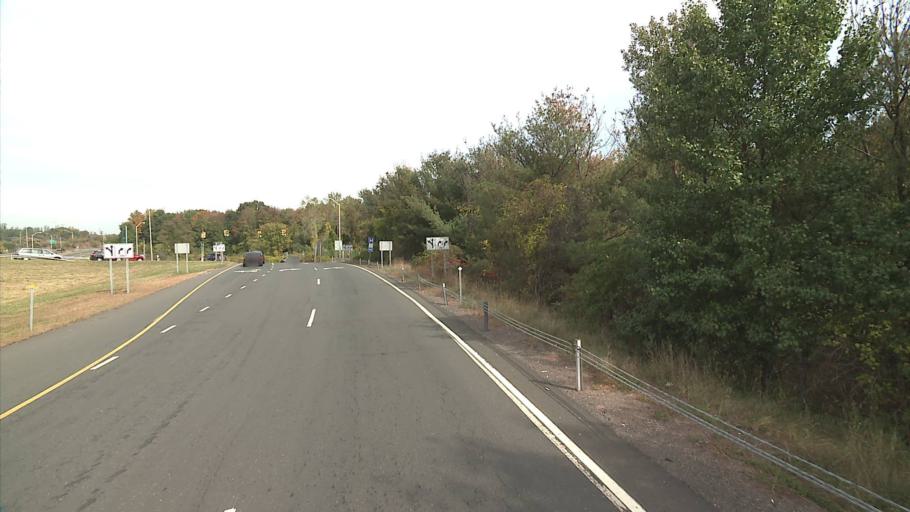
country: US
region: Connecticut
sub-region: Hartford County
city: East Hartford
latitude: 41.7793
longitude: -72.5686
